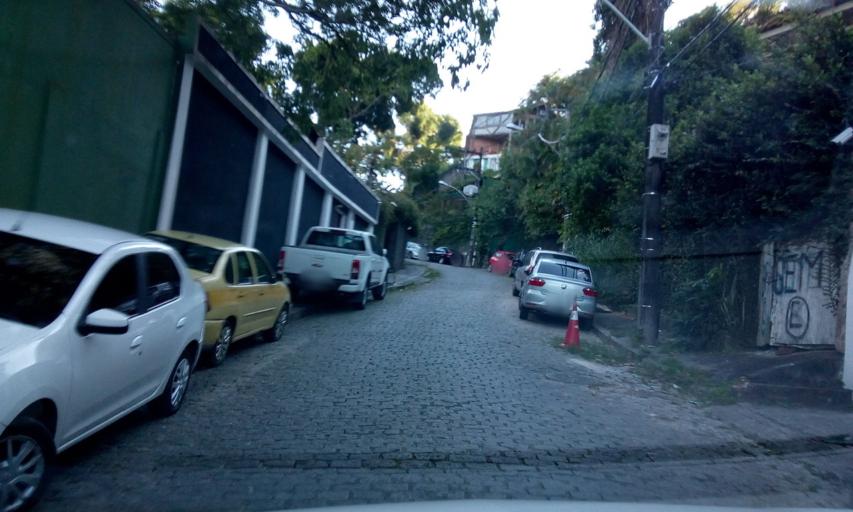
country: BR
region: Rio de Janeiro
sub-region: Rio De Janeiro
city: Rio de Janeiro
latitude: -22.9656
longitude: -43.1980
